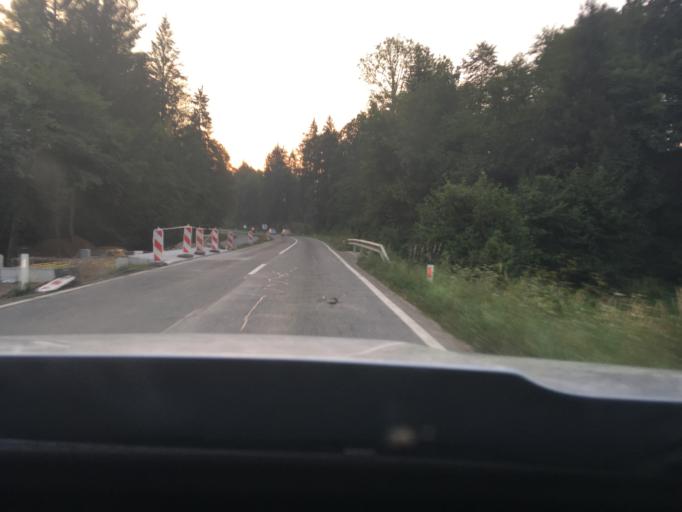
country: SI
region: Kocevje
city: Kocevje
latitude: 45.6804
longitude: 14.8226
